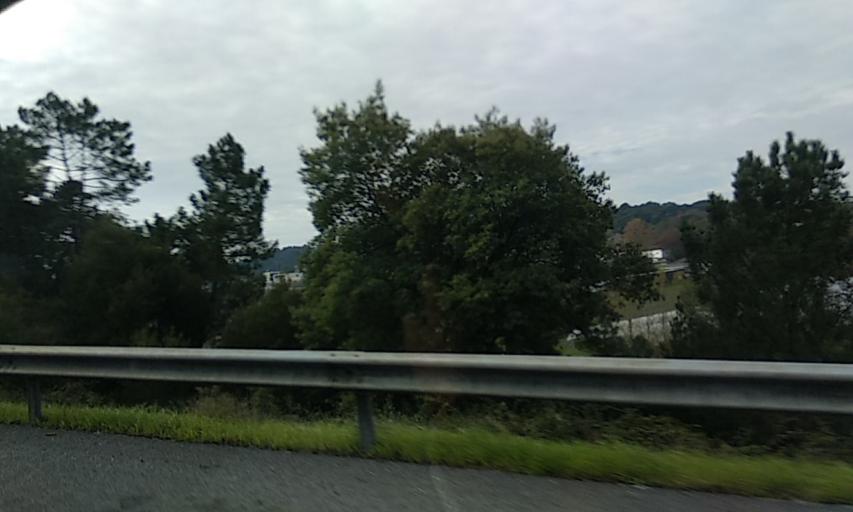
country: PT
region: Porto
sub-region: Santo Tirso
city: Santo Tirso
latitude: 41.3667
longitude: -8.5018
